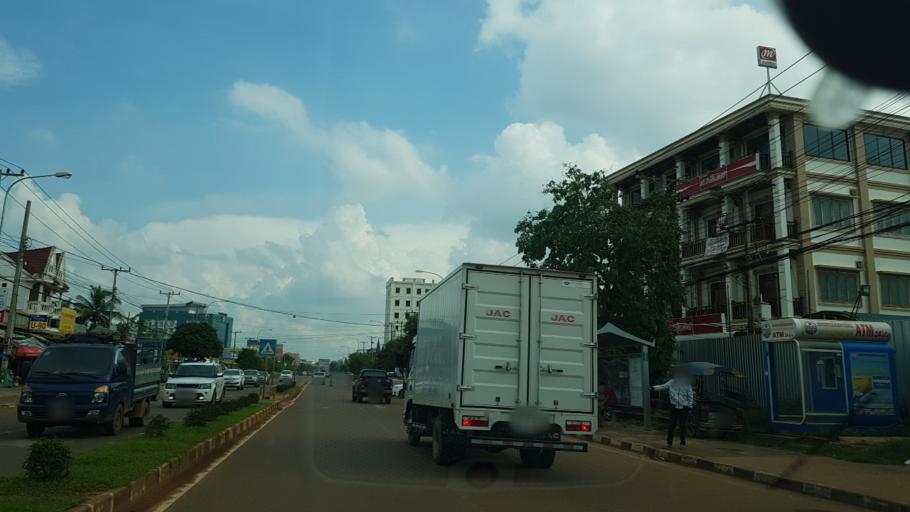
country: LA
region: Vientiane
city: Vientiane
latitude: 18.0290
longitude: 102.6517
